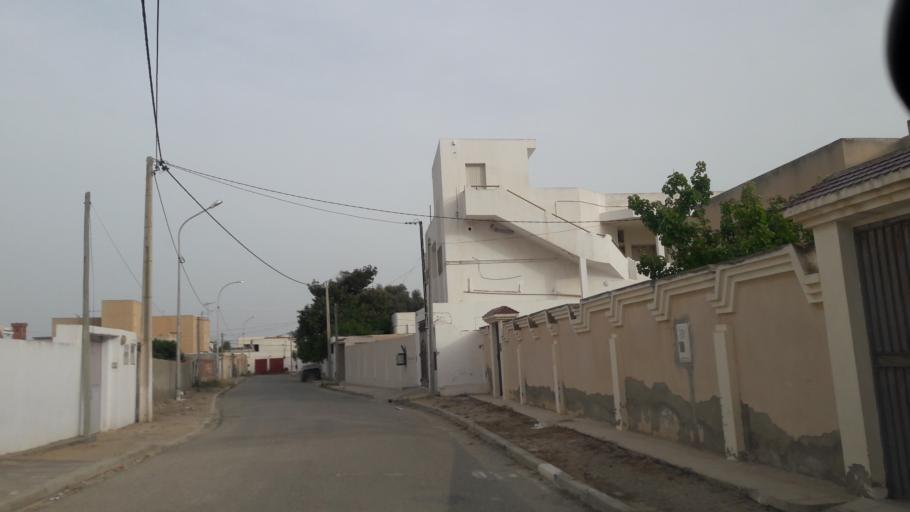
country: TN
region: Safaqis
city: Al Qarmadah
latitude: 34.7757
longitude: 10.7653
